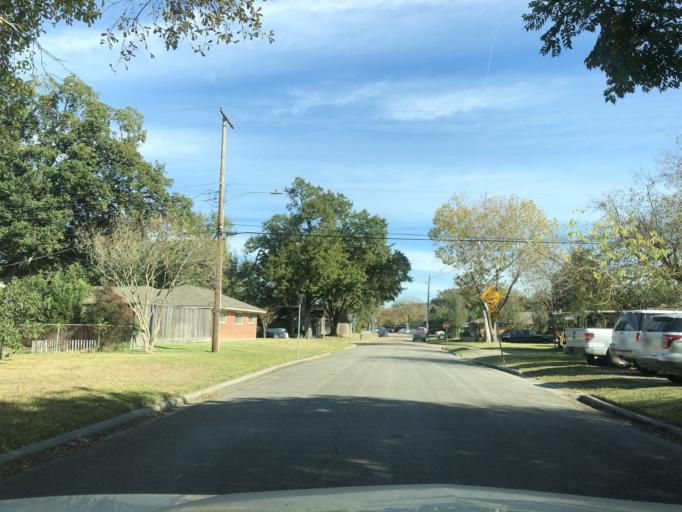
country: US
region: Texas
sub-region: Harris County
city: Bellaire
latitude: 29.6823
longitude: -95.5117
